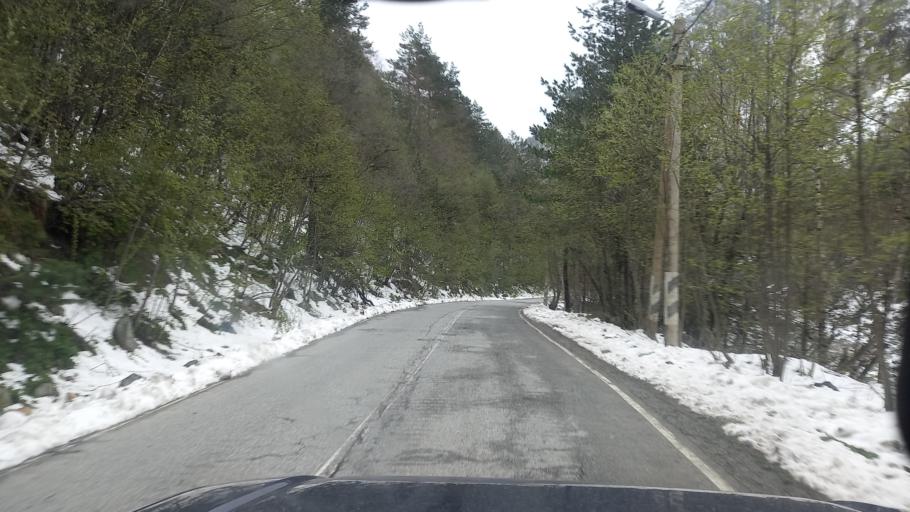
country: RU
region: North Ossetia
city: Mizur
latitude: 42.7914
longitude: 43.9111
